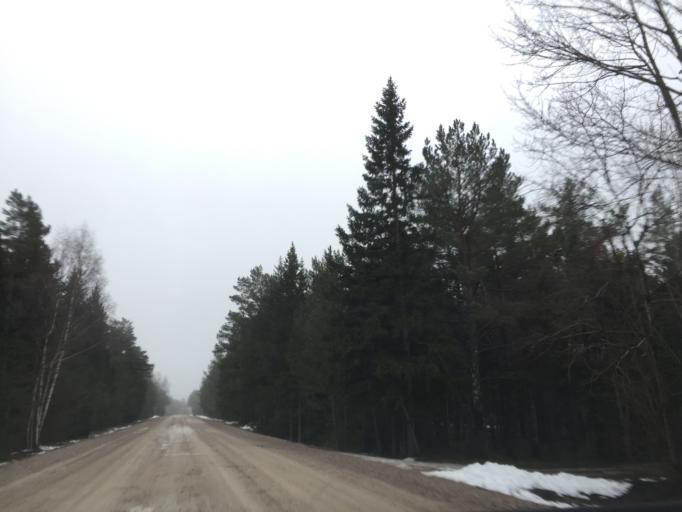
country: EE
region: Saare
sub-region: Kuressaare linn
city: Kuressaare
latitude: 58.4806
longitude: 21.9995
